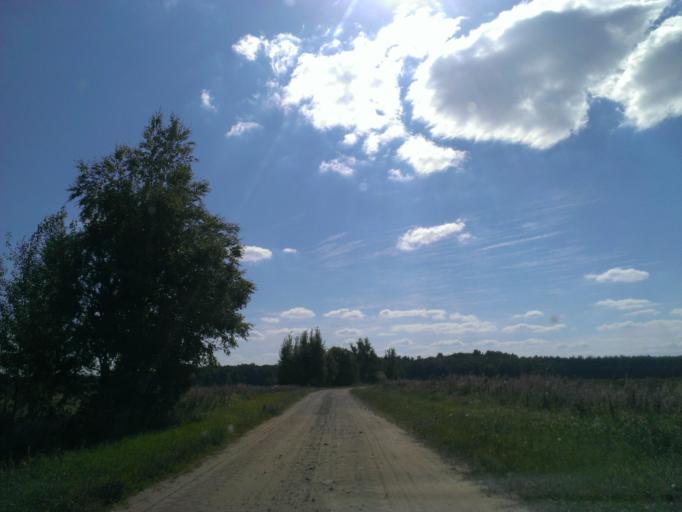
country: LV
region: Riga
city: Jaunciems
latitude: 57.0848
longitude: 24.2115
